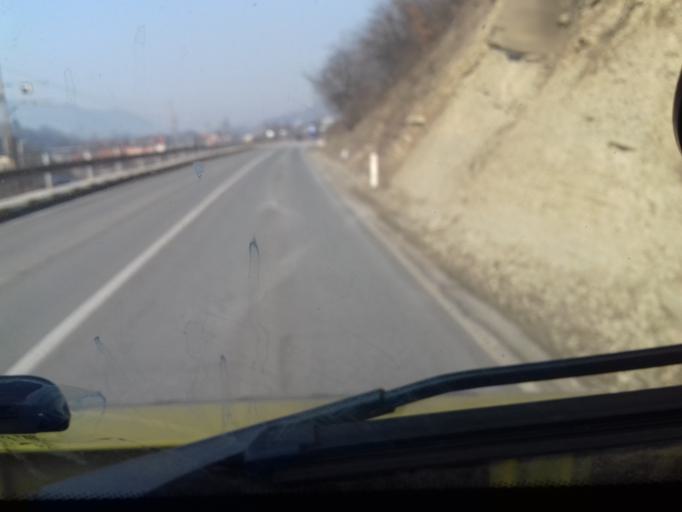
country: BA
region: Federation of Bosnia and Herzegovina
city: Vogosca
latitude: 43.9110
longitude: 18.3242
